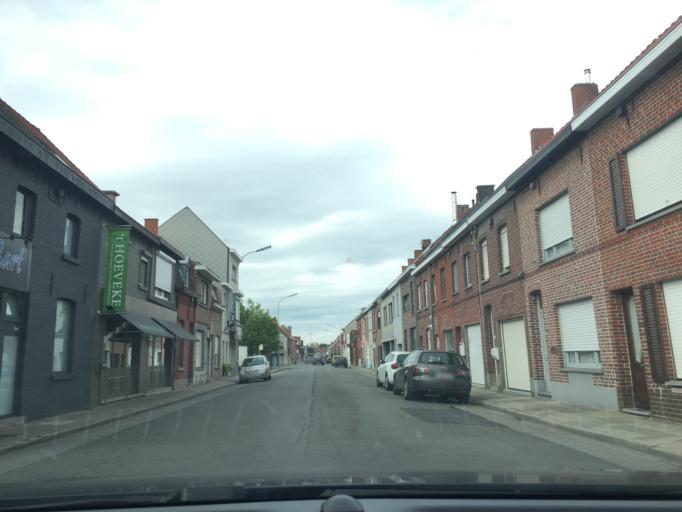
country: BE
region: Flanders
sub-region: Provincie West-Vlaanderen
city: Izegem
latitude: 50.9091
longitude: 3.2188
